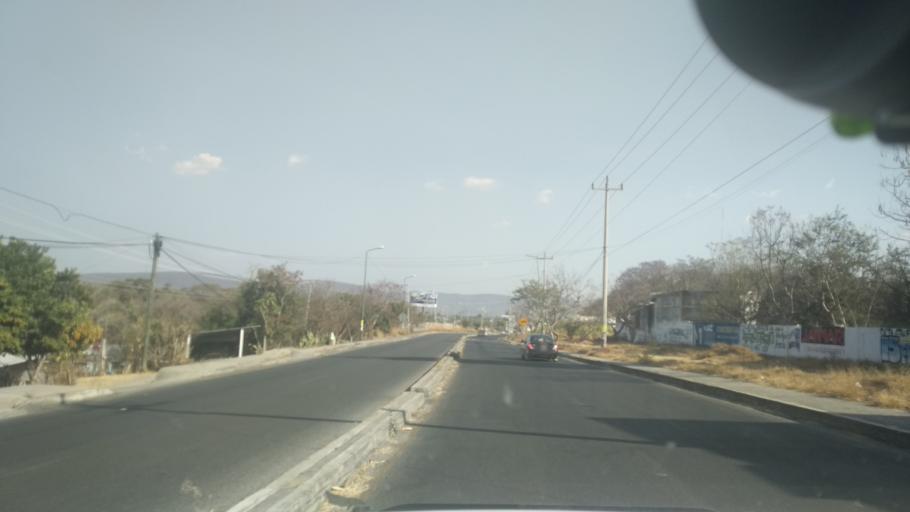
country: MX
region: Puebla
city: Izucar de Matamoros
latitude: 18.6189
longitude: -98.4703
